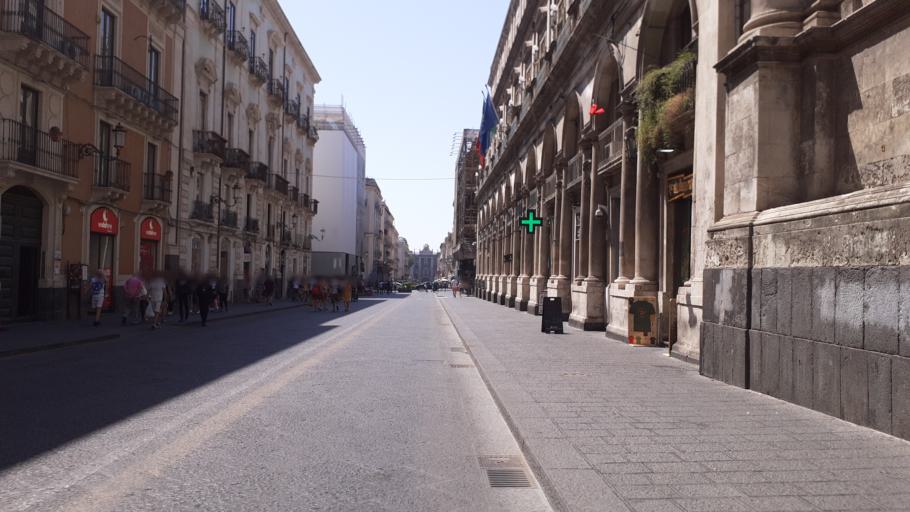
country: IT
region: Sicily
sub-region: Catania
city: Catania
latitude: 37.5061
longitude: 15.0865
